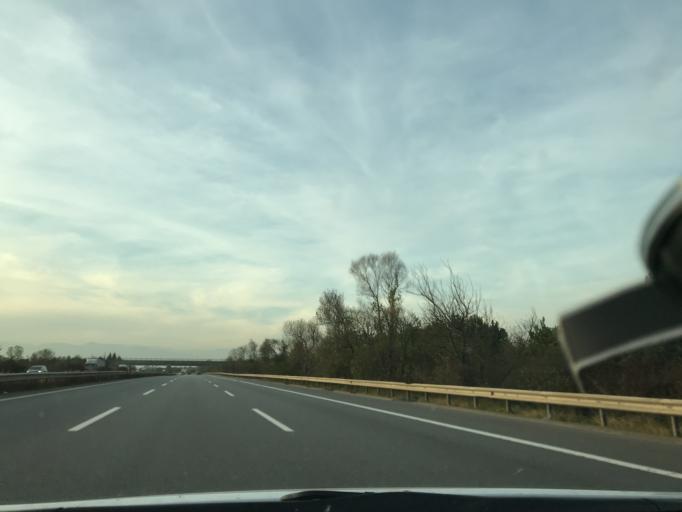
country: TR
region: Duzce
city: Cilimli
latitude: 40.8402
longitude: 31.0264
